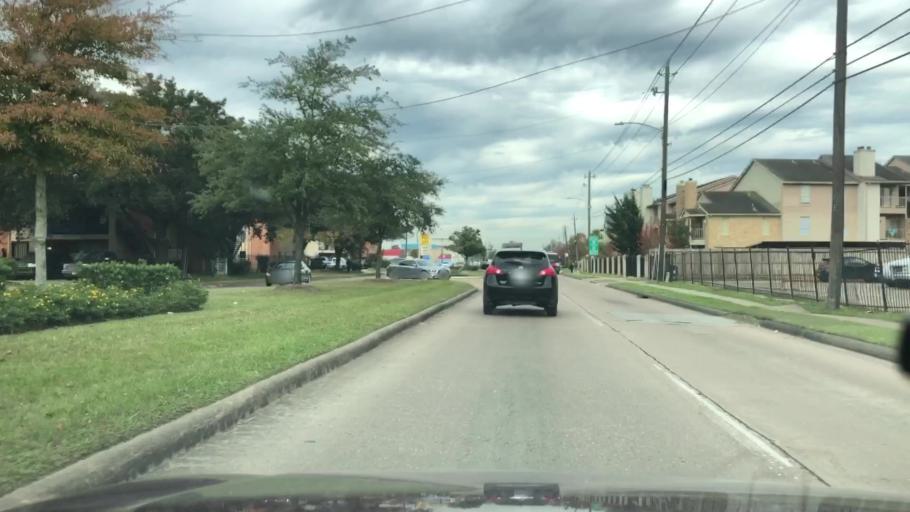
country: US
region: Texas
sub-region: Fort Bend County
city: Missouri City
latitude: 29.6683
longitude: -95.5281
